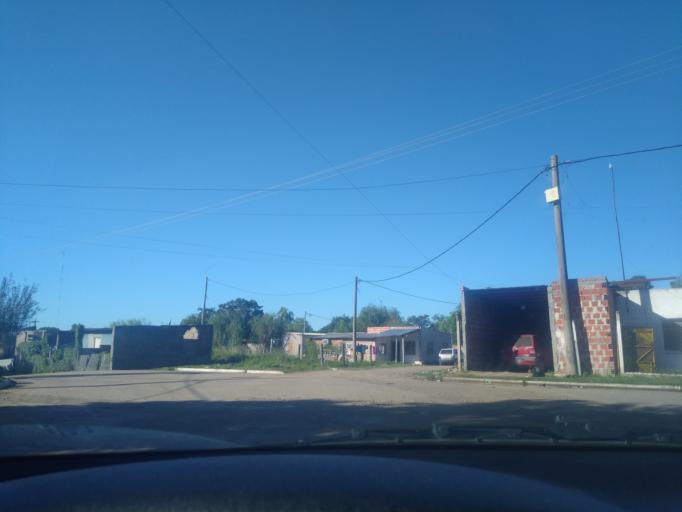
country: AR
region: Chaco
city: Puerto Vilelas
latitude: -27.5095
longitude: -58.9373
